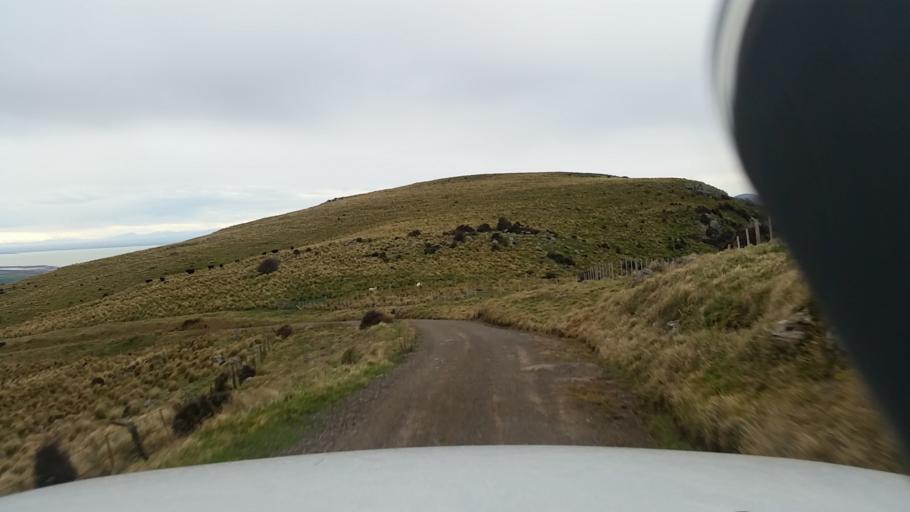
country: NZ
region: Canterbury
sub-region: Christchurch City
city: Christchurch
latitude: -43.8154
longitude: 172.7573
